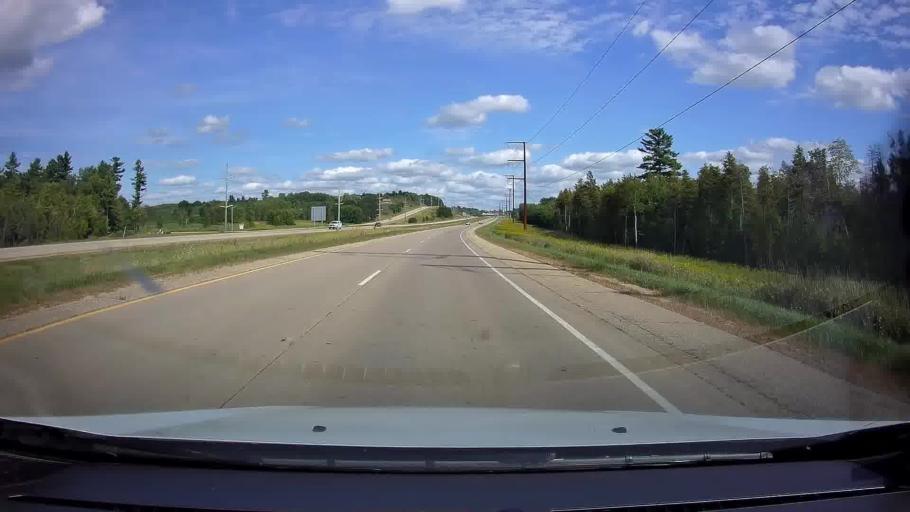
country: US
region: Wisconsin
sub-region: Shawano County
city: Shawano
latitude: 44.7609
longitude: -88.5508
